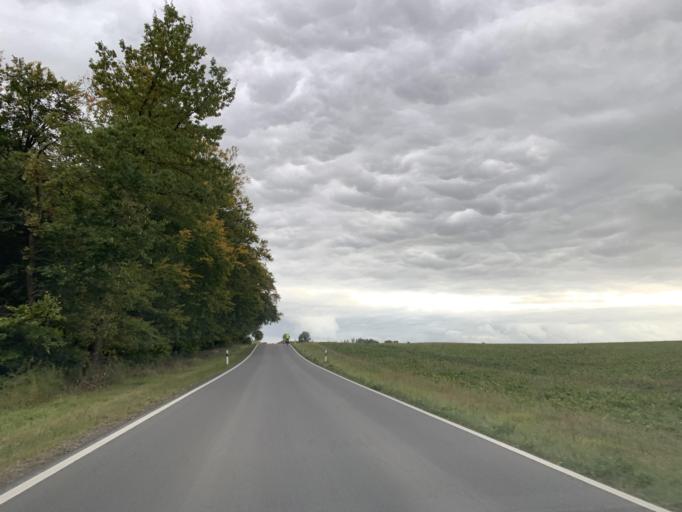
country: DE
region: Mecklenburg-Vorpommern
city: Burg Stargard
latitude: 53.4731
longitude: 13.2932
